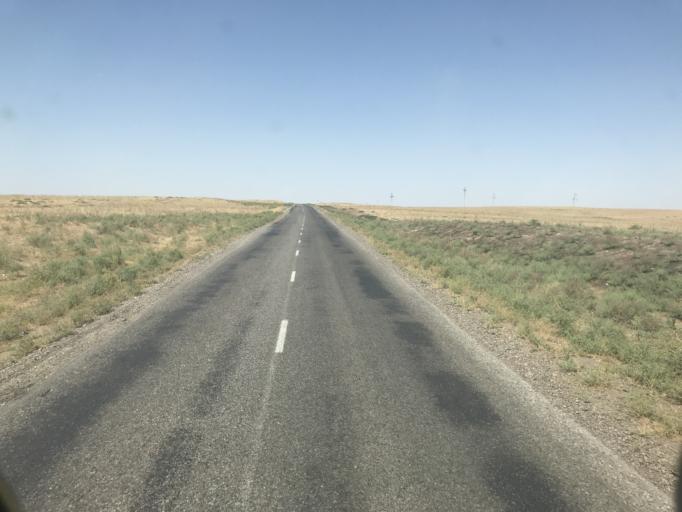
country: UZ
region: Toshkent
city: Chinoz
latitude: 41.1564
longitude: 68.6682
